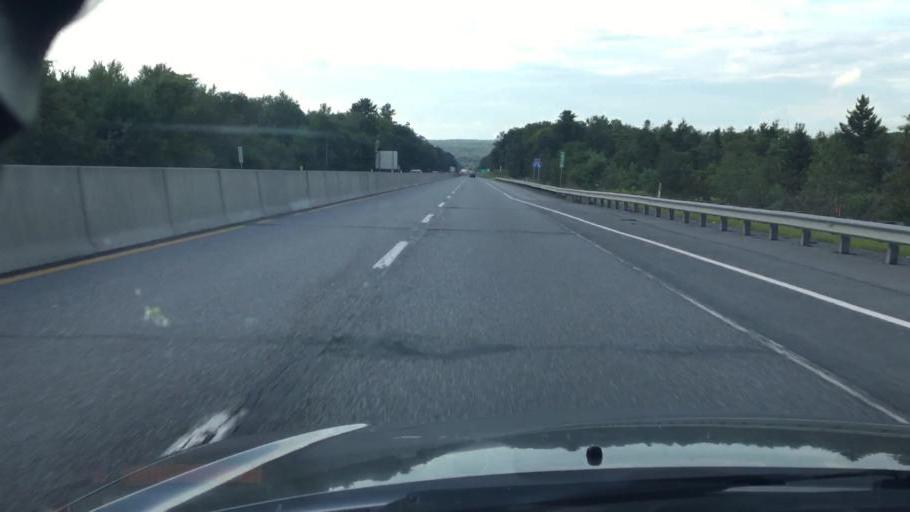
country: US
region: Pennsylvania
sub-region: Carbon County
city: Towamensing Trails
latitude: 40.9905
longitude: -75.6314
